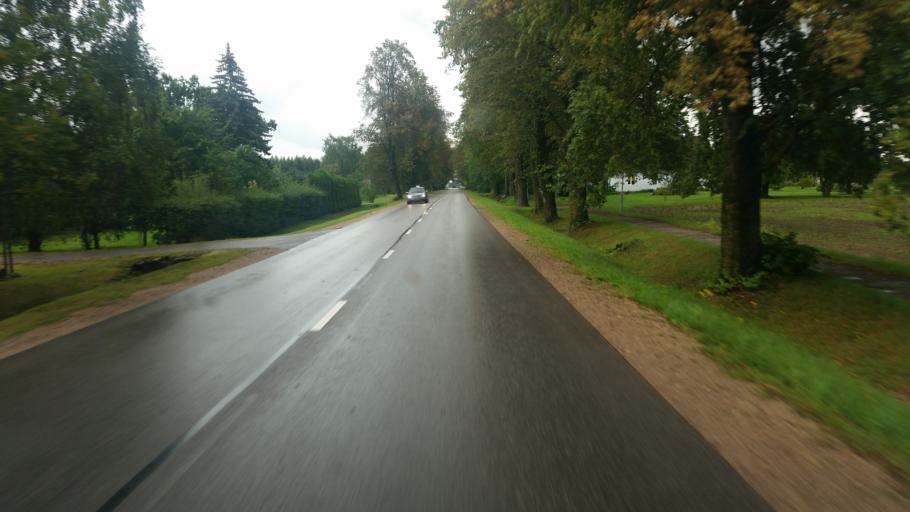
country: LV
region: Bauskas Rajons
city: Bauska
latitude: 56.4323
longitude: 24.3443
